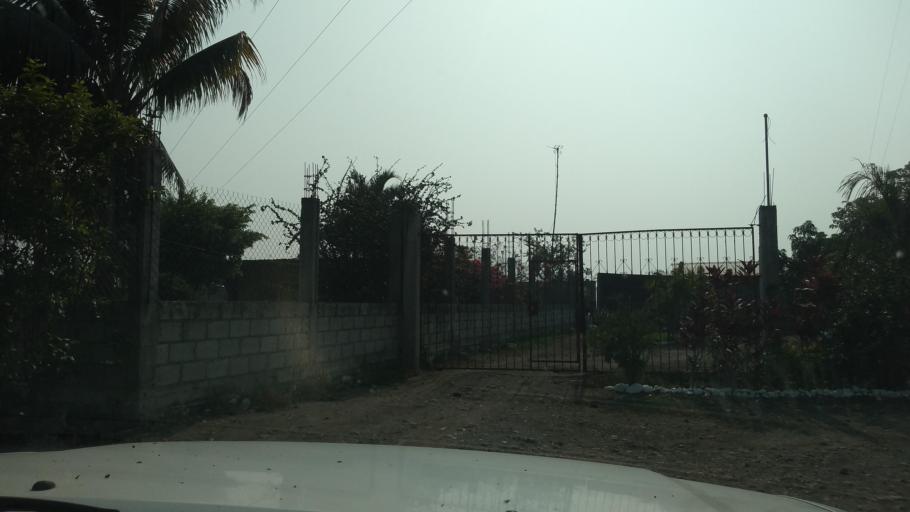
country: MX
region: Oaxaca
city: Acatlan de Perez Figueroa
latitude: 18.6234
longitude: -96.6004
